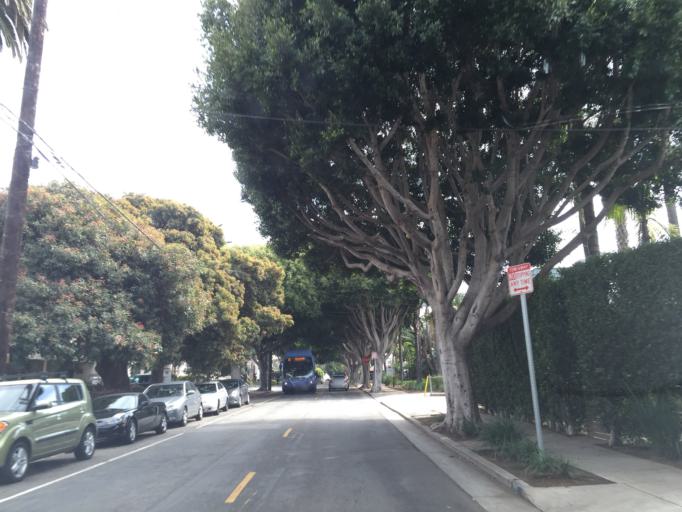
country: US
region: California
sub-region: Los Angeles County
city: Santa Monica
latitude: 34.0010
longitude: -118.4785
